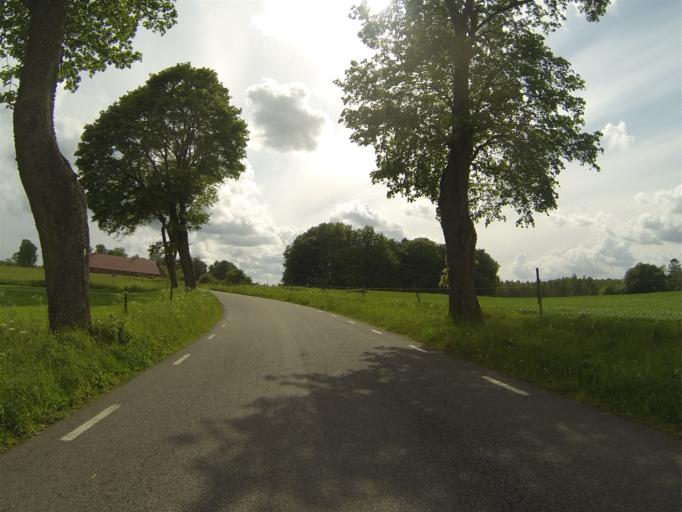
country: SE
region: Skane
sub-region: Sjobo Kommun
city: Blentarp
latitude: 55.6513
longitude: 13.6014
